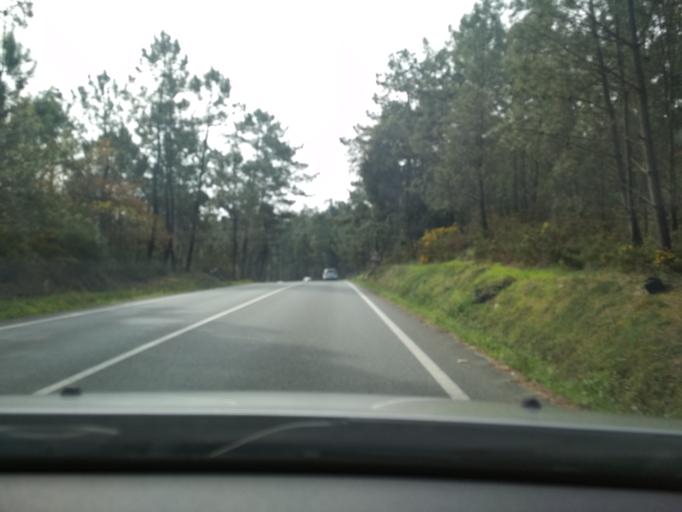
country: ES
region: Galicia
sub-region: Provincia de Pontevedra
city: Catoira
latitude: 42.6741
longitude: -8.7147
